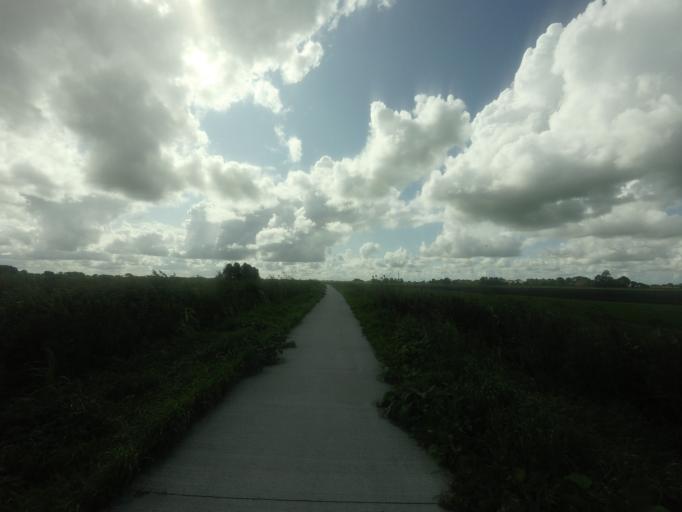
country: NL
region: Friesland
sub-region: Gemeente Littenseradiel
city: Makkum
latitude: 53.0913
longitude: 5.7107
